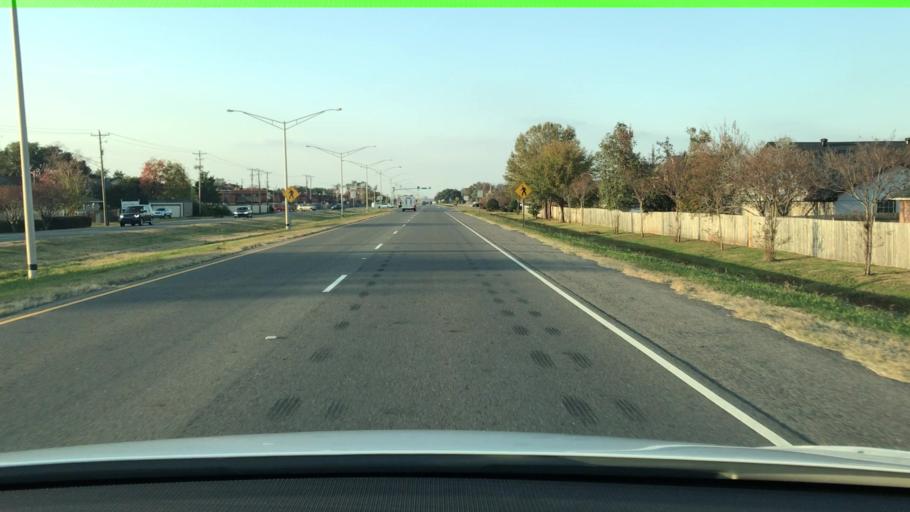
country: US
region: Louisiana
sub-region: Bossier Parish
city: Bossier City
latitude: 32.4109
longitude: -93.6996
